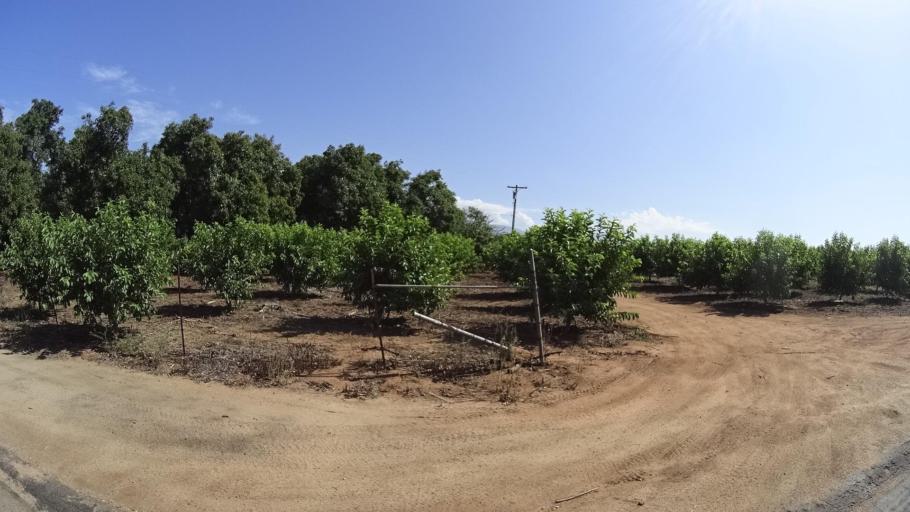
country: US
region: California
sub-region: San Diego County
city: Valley Center
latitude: 33.3082
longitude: -117.0503
